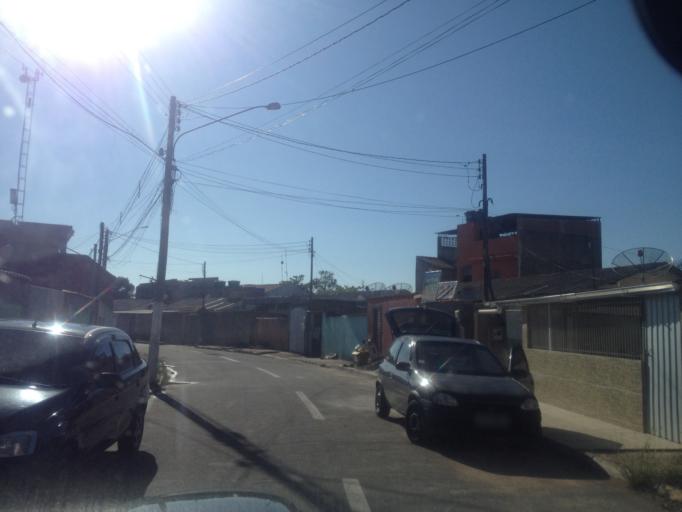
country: BR
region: Rio de Janeiro
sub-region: Porto Real
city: Porto Real
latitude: -22.4149
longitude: -44.3060
